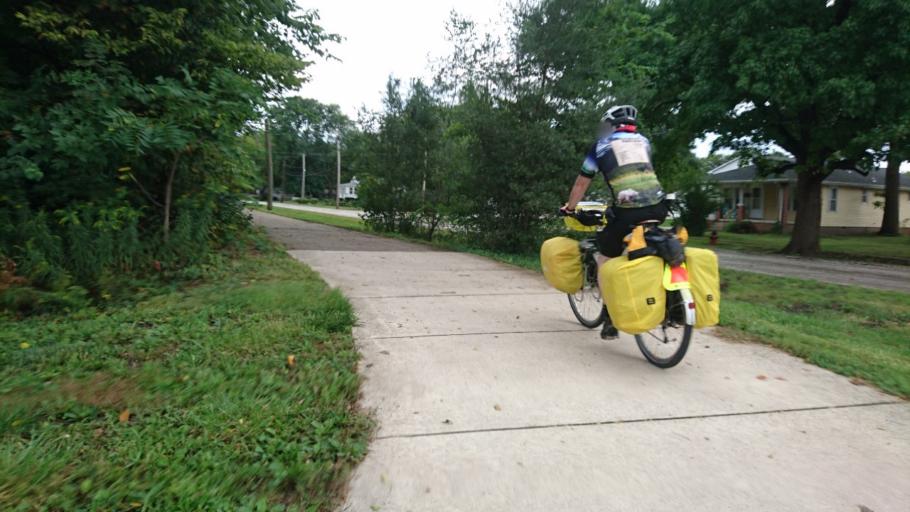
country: US
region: Illinois
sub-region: Sangamon County
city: Jerome
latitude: 39.7624
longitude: -89.6680
